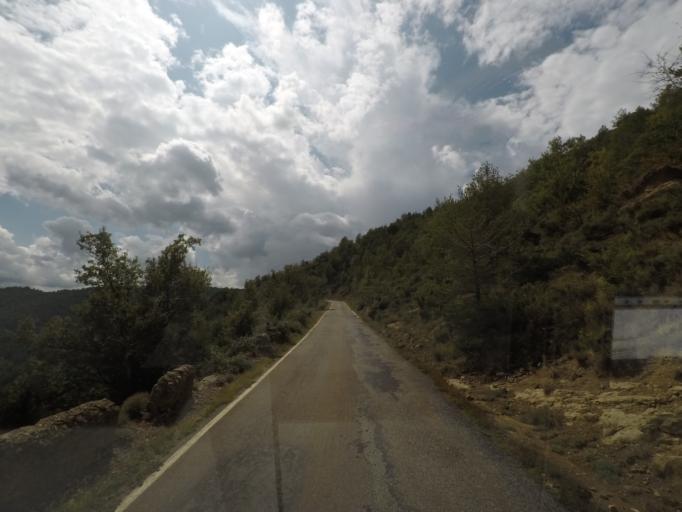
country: ES
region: Aragon
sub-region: Provincia de Huesca
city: Boltana
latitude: 42.4054
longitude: -0.0083
